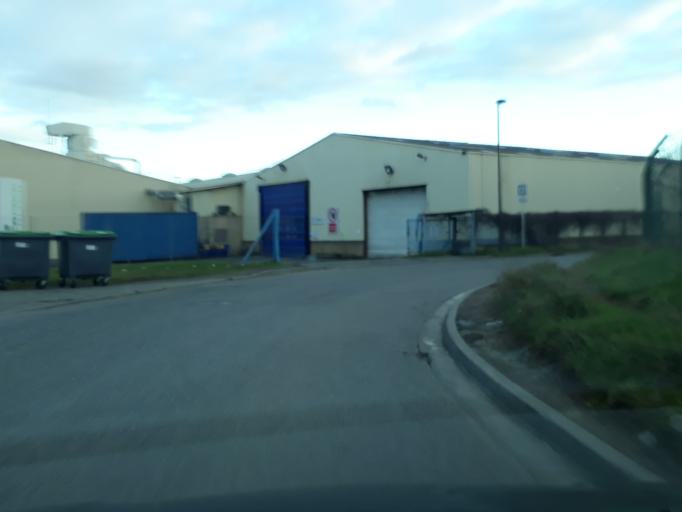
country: FR
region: Midi-Pyrenees
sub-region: Departement de la Haute-Garonne
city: Portet-sur-Garonne
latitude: 43.5521
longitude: 1.4177
